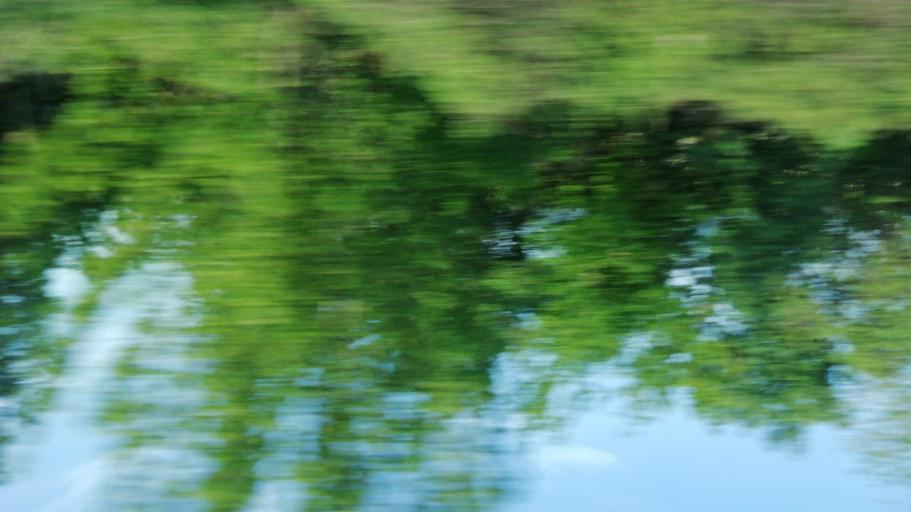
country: TR
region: Manisa
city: Saruhanli
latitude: 38.7395
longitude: 27.6002
